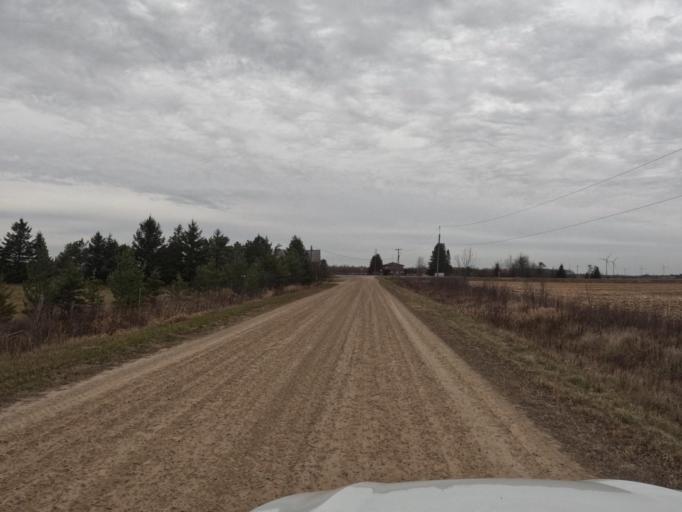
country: CA
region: Ontario
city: Shelburne
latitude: 44.0381
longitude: -80.3729
